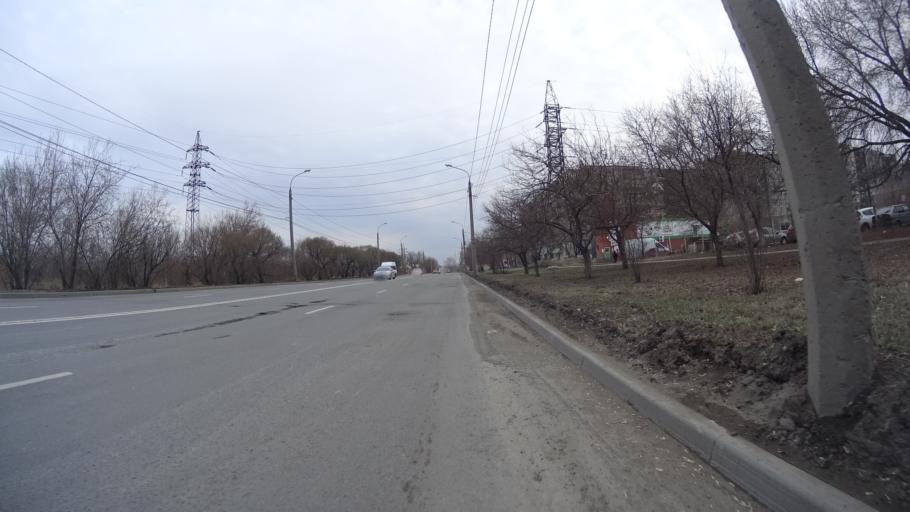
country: RU
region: Chelyabinsk
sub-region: Gorod Chelyabinsk
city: Chelyabinsk
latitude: 55.1826
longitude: 61.4862
